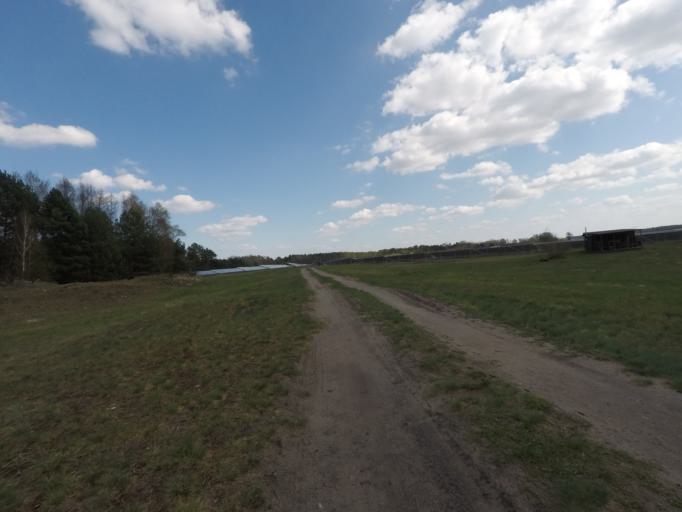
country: DE
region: Brandenburg
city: Melchow
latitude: 52.8327
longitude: 13.7016
